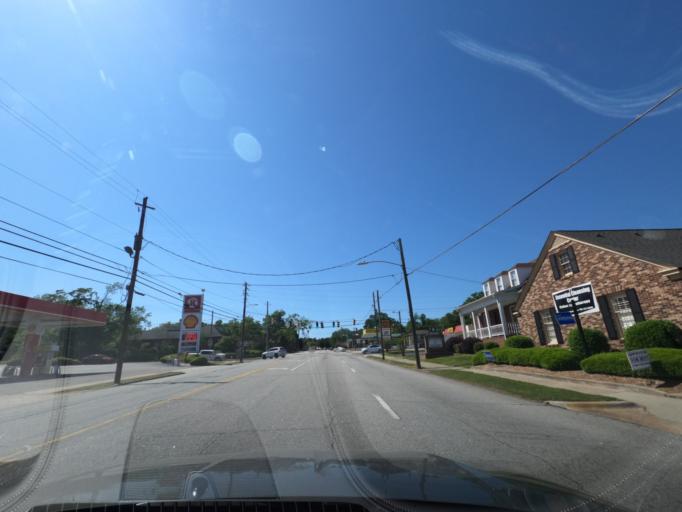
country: US
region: Georgia
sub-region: Richmond County
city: Augusta
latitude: 33.4694
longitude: -82.0094
